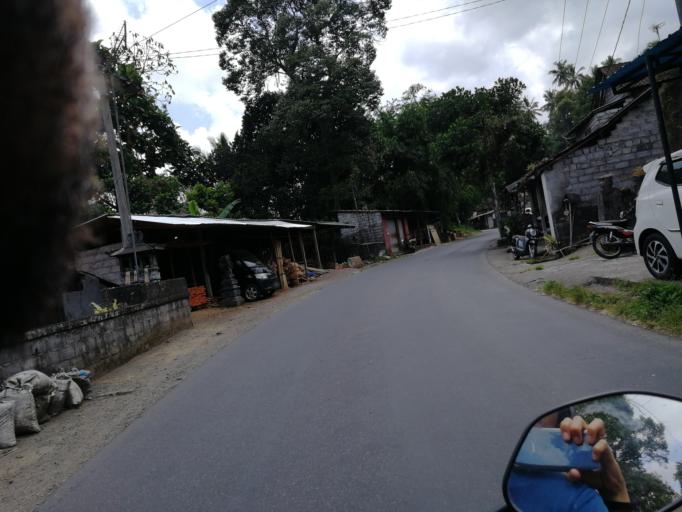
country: ID
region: Bali
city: Banjar Wates Tengah
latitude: -8.4532
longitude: 115.4531
